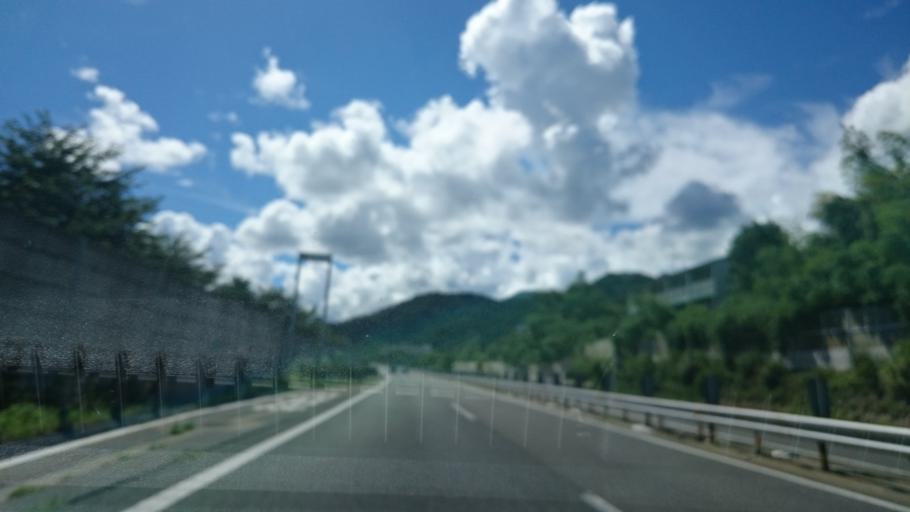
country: JP
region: Nagano
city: Iida
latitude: 35.4869
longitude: 137.7815
